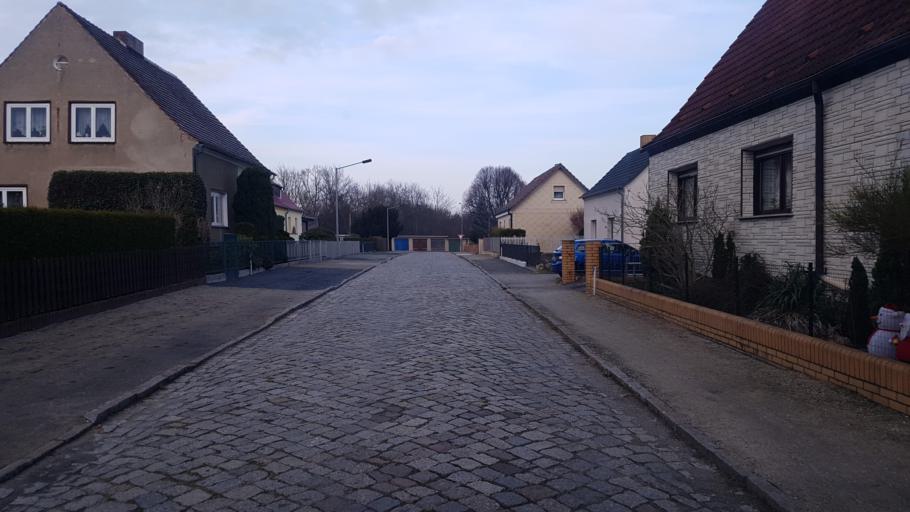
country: DE
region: Brandenburg
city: Lauchhammer
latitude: 51.5005
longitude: 13.7599
